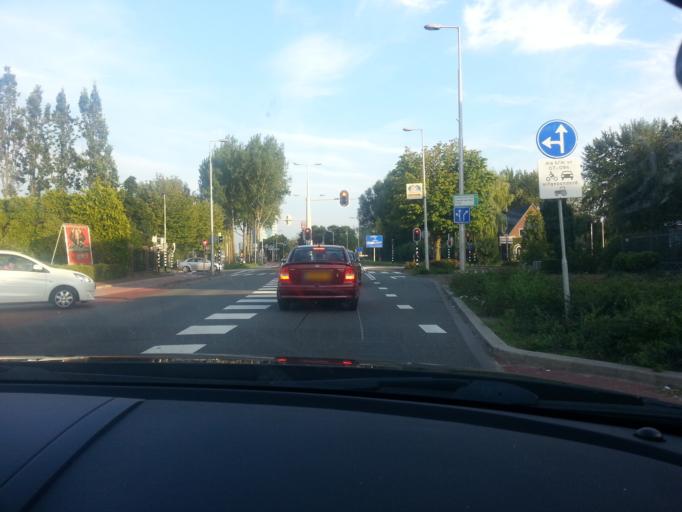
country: NL
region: South Holland
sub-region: Gemeente Capelle aan den IJssel
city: Capelle aan den IJssel
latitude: 51.9351
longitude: 4.5821
